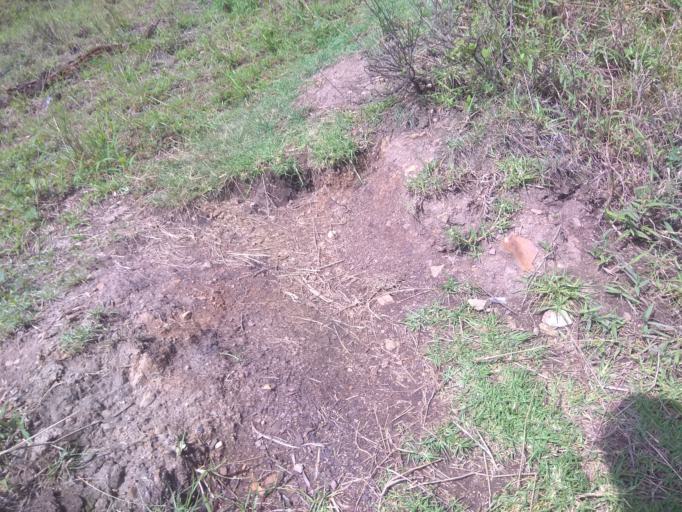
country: CO
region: Boyaca
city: Socha Viejo
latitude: 5.9831
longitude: -72.7143
